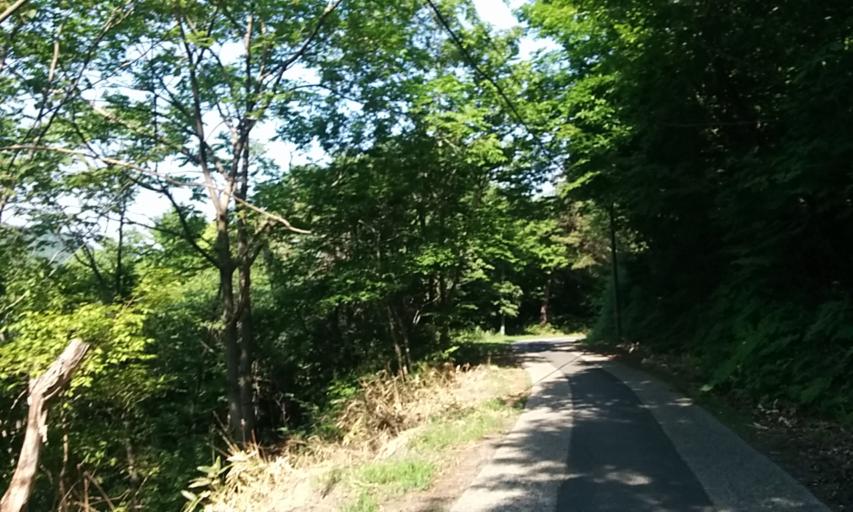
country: JP
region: Kyoto
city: Miyazu
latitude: 35.5872
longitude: 135.1922
